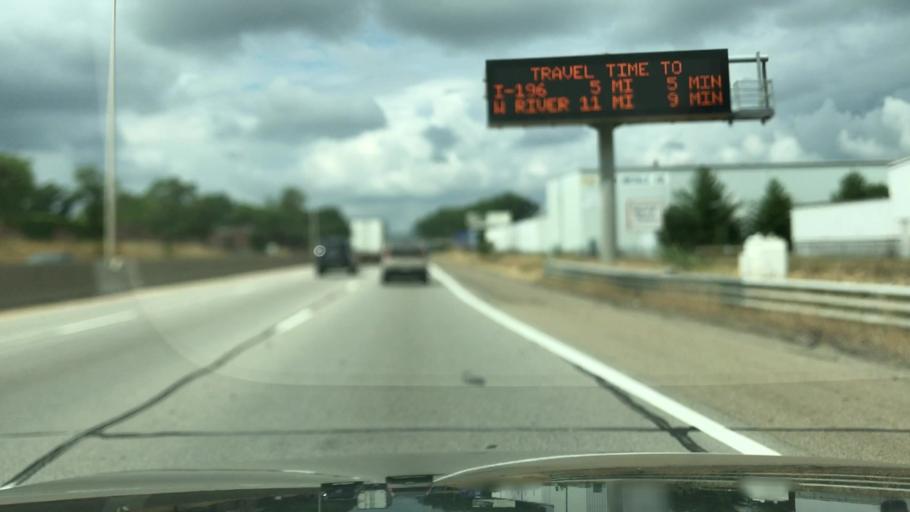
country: US
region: Michigan
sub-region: Kent County
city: Wyoming
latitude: 42.9028
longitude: -85.6773
